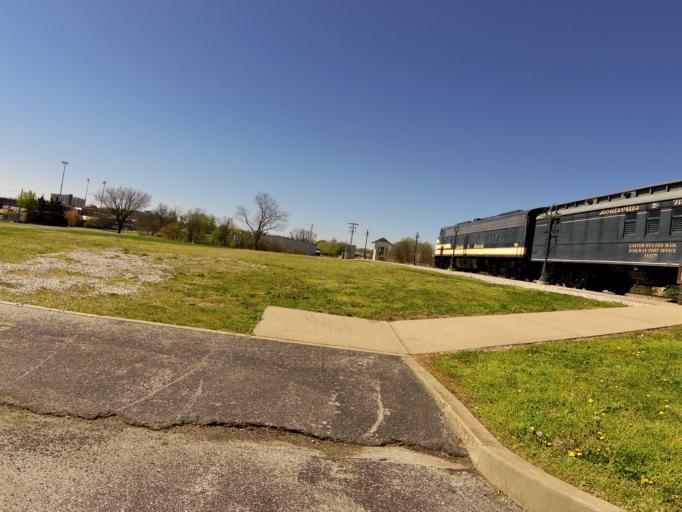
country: US
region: Kentucky
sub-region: Warren County
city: Bowling Green
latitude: 36.9998
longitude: -86.4391
